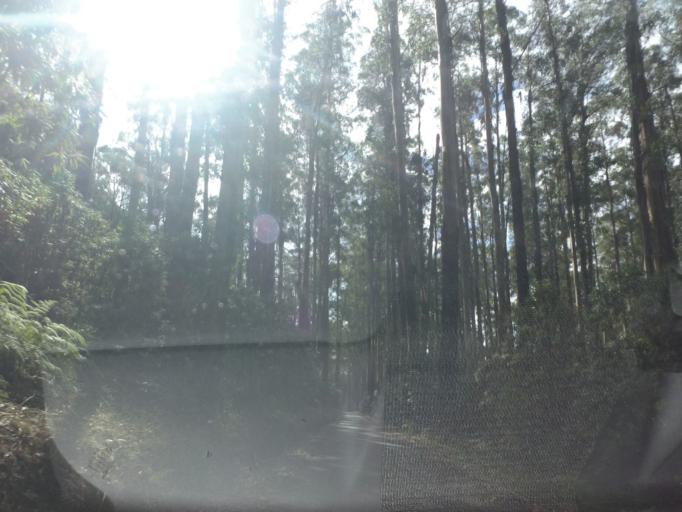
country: AU
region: Victoria
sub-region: Yarra Ranges
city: Millgrove
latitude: -37.5819
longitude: 145.6935
